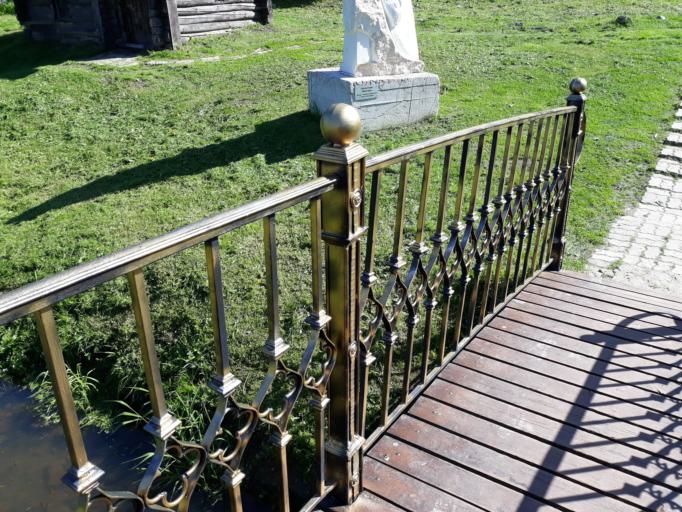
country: RU
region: Jaroslavl
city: Krasnyy Profintern
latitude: 57.8650
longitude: 40.2694
